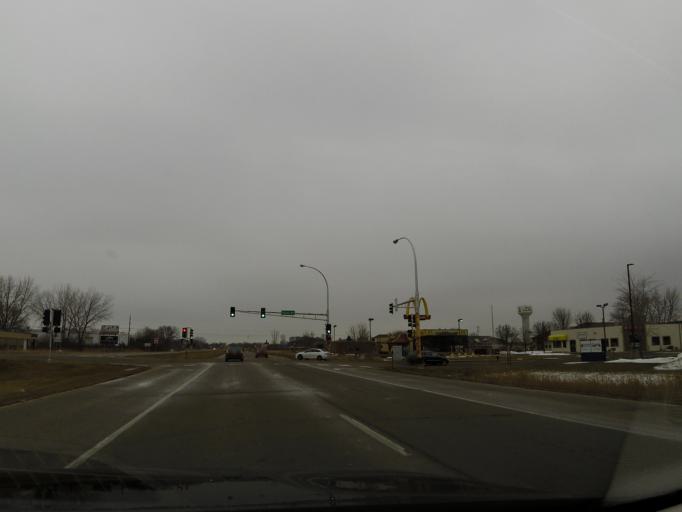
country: US
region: Minnesota
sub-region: Carver County
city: Norwood Young America
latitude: 44.7713
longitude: -93.9204
